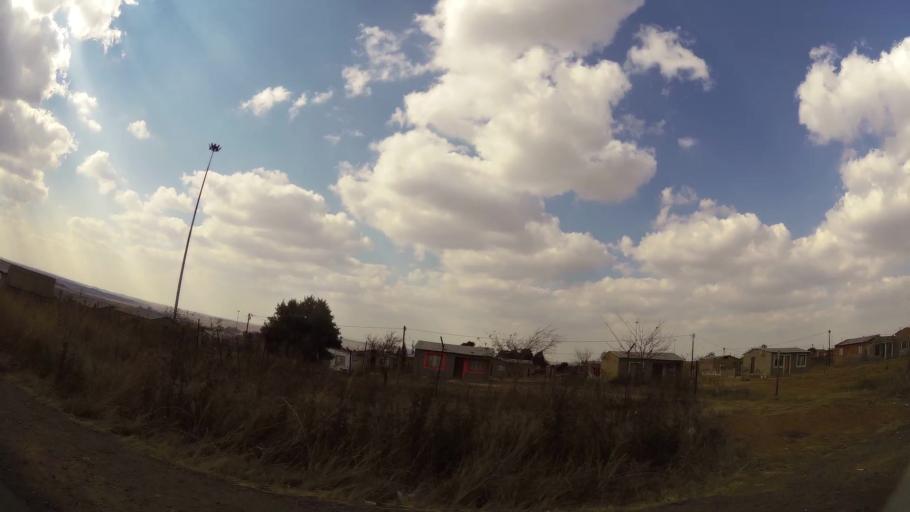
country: ZA
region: Mpumalanga
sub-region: Nkangala District Municipality
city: Delmas
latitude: -26.0950
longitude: 28.6775
